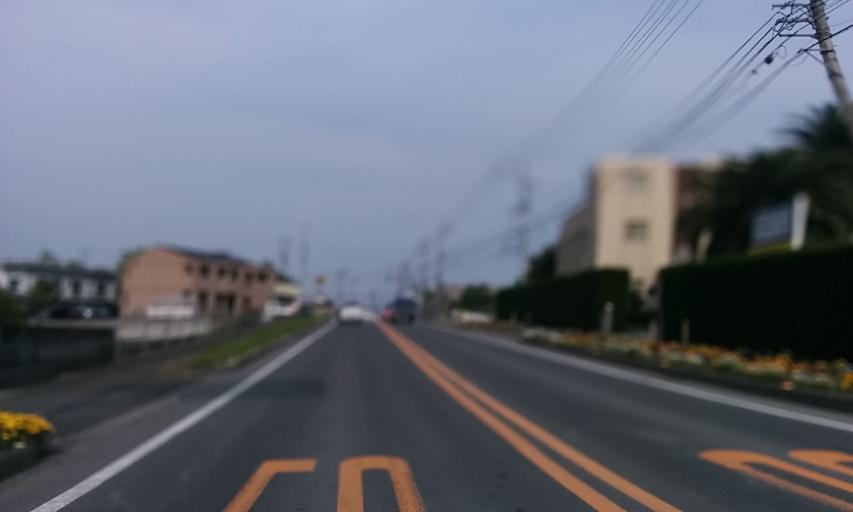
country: JP
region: Ehime
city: Kawanoecho
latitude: 33.9672
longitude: 133.4844
